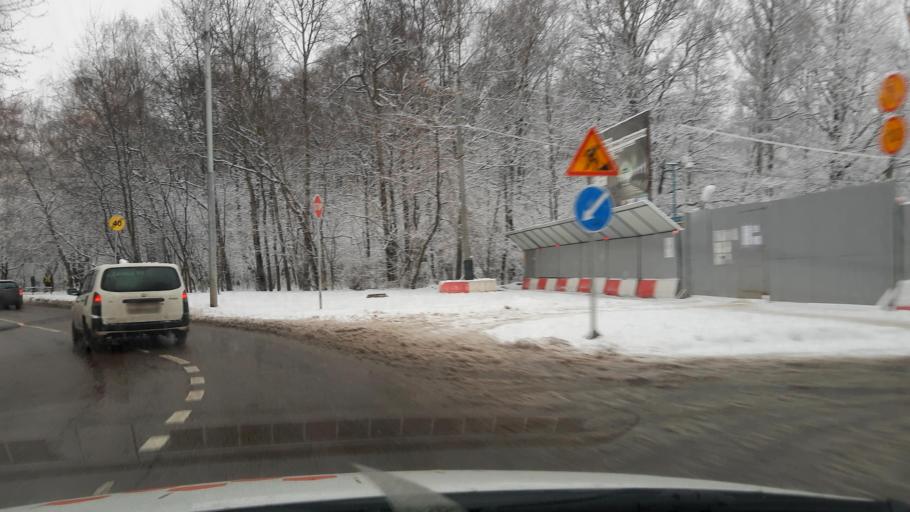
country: RU
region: Moscow
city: Tyoply Stan
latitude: 55.6253
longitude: 37.4830
